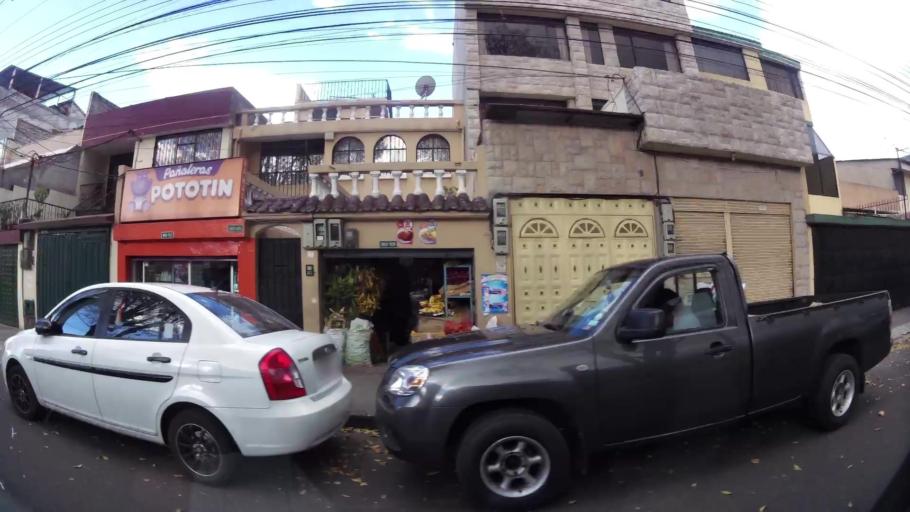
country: EC
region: Pichincha
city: Quito
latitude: -0.1250
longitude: -78.4861
